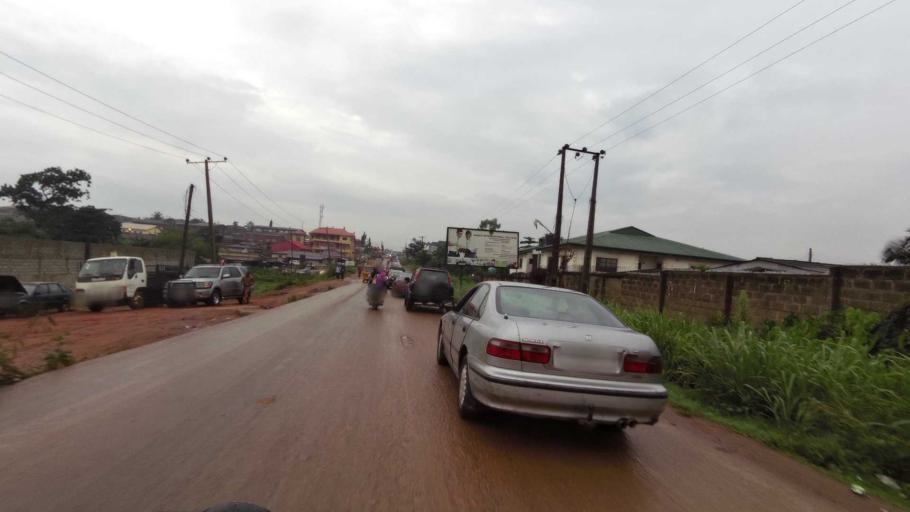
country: NG
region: Oyo
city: Ibadan
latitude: 7.4280
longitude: 3.9390
